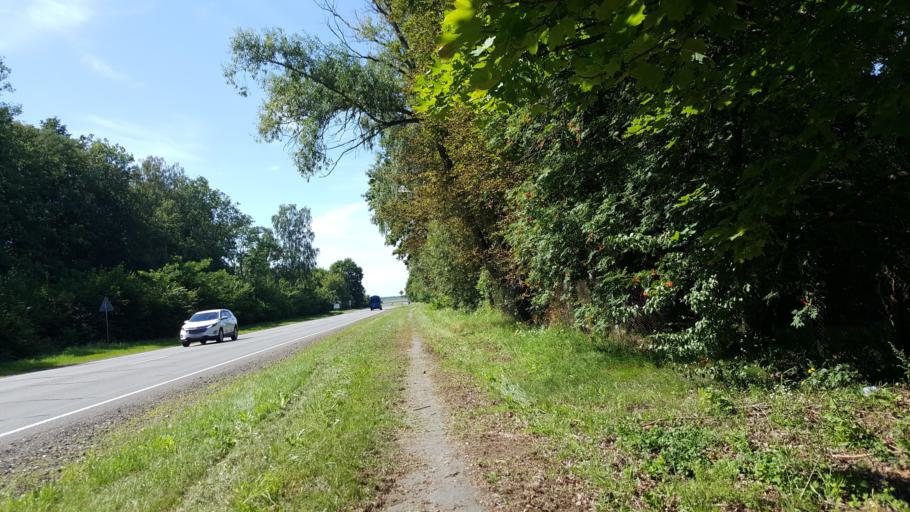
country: BY
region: Brest
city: Charnawchytsy
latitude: 52.2637
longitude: 23.7639
